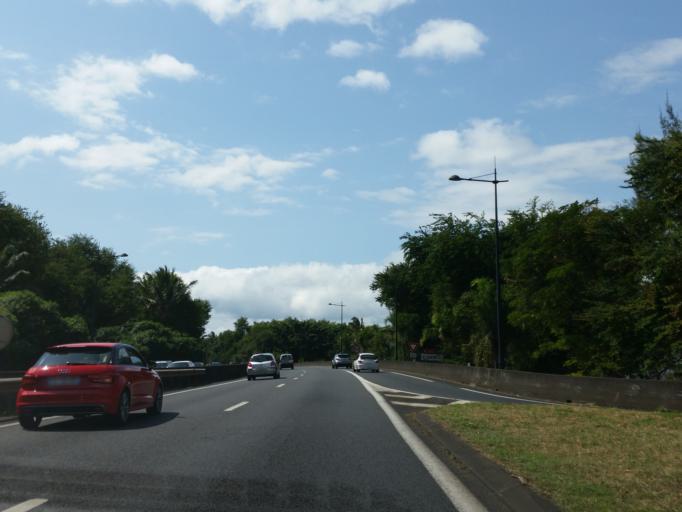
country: RE
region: Reunion
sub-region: Reunion
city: Saint-Denis
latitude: -20.8868
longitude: 55.4896
